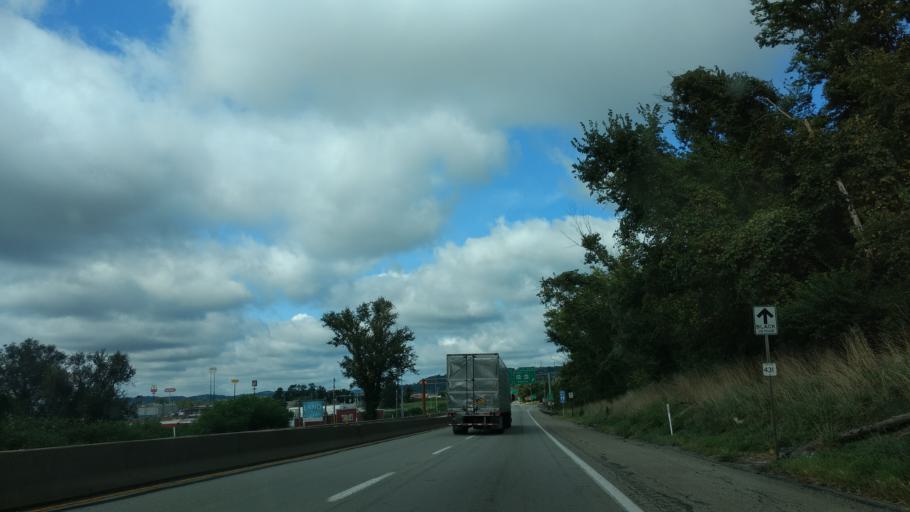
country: US
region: Pennsylvania
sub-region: Westmoreland County
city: Lynnwood-Pricedale
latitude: 40.1401
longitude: -79.8364
